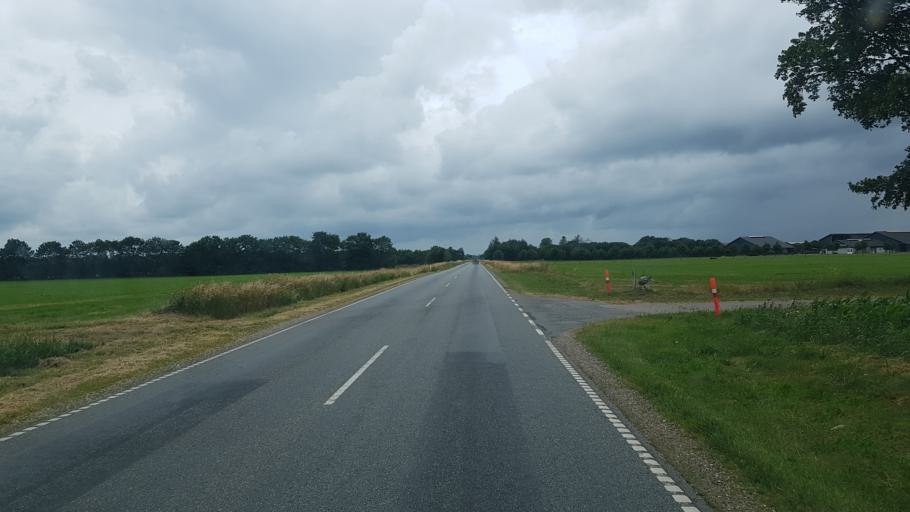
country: DK
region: South Denmark
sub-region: Kolding Kommune
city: Vamdrup
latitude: 55.4337
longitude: 9.2150
